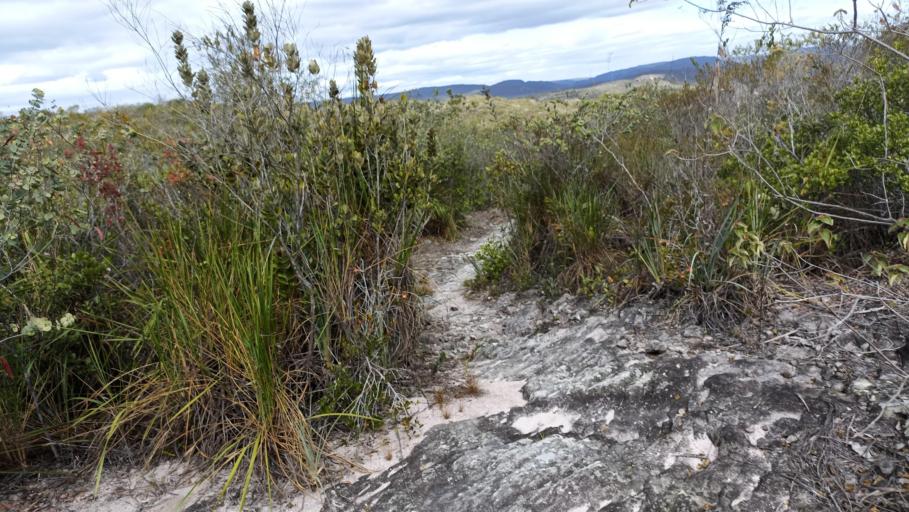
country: BR
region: Bahia
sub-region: Andarai
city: Vera Cruz
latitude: -12.9957
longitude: -41.3768
